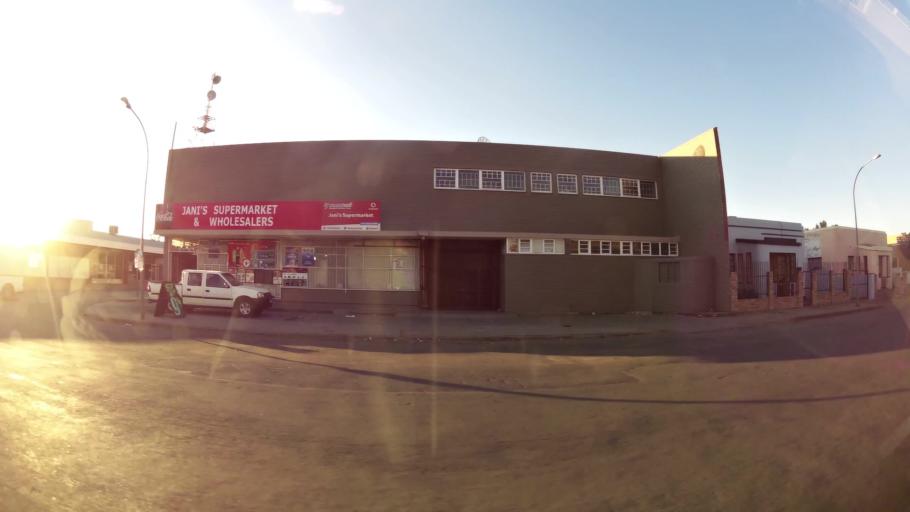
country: ZA
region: Northern Cape
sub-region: Frances Baard District Municipality
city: Kimberley
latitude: -28.7372
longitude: 24.7714
